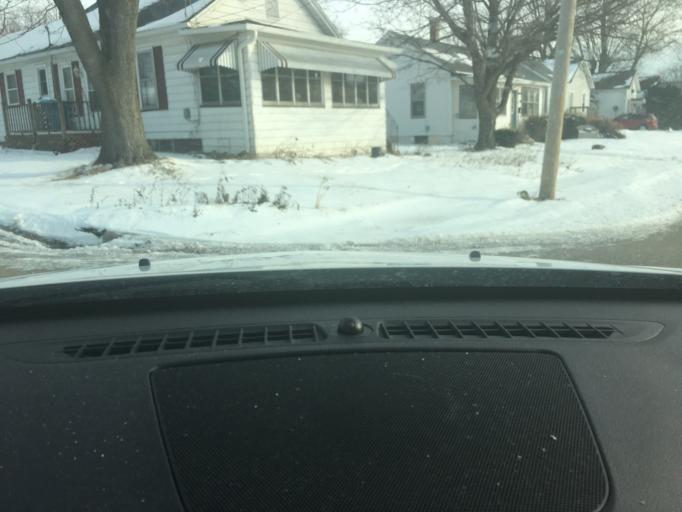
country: US
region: Illinois
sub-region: LaSalle County
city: Peru
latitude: 41.3298
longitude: -89.1155
